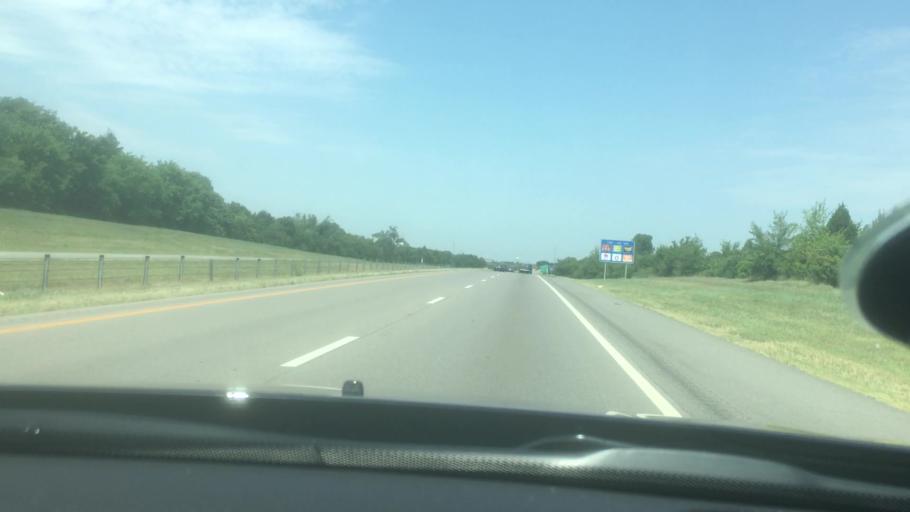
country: US
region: Oklahoma
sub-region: Oklahoma County
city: Midwest City
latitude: 35.4230
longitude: -97.3441
